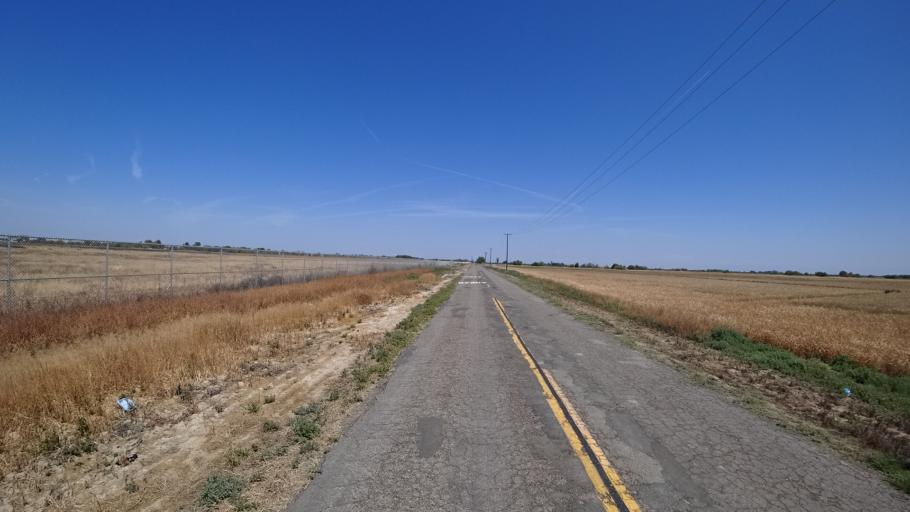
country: US
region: California
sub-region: Kings County
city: Lemoore
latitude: 36.2267
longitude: -119.7446
